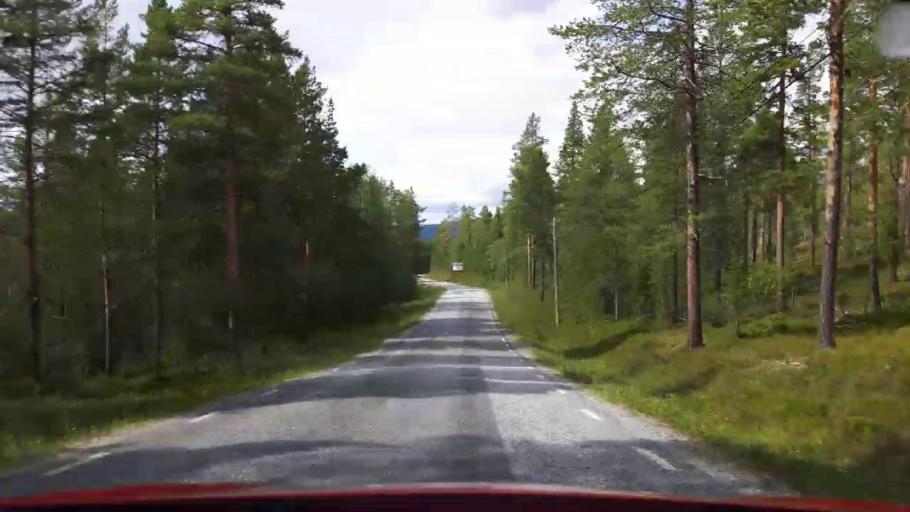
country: NO
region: Hedmark
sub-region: Engerdal
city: Engerdal
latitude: 62.4191
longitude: 12.6958
